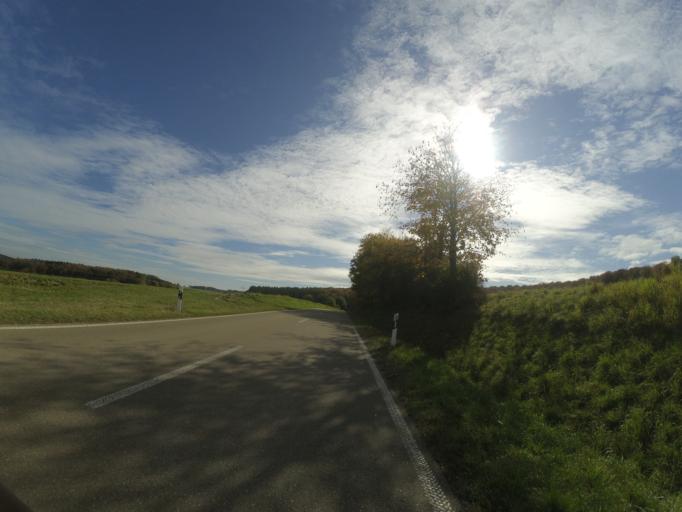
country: DE
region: Baden-Wuerttemberg
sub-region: Tuebingen Region
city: Amstetten
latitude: 48.6111
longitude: 9.9213
